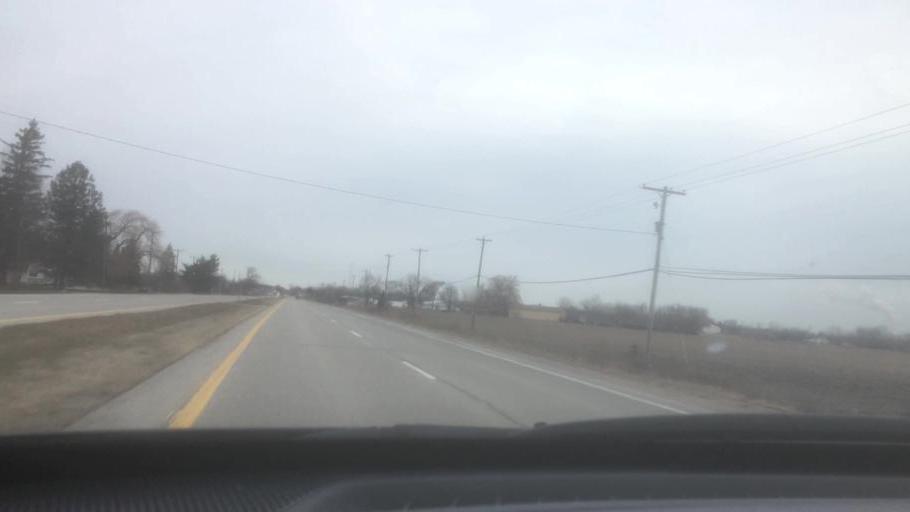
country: US
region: Michigan
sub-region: Bay County
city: Essexville
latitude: 43.5689
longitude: -83.8473
